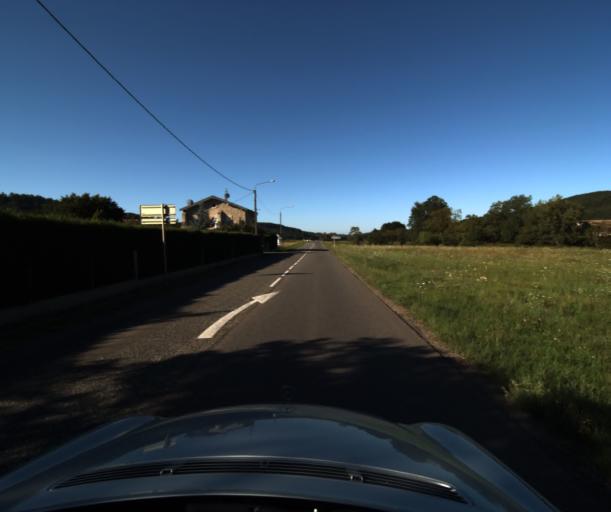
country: FR
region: Midi-Pyrenees
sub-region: Departement de l'Ariege
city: Lavelanet
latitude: 42.9973
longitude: 1.8797
